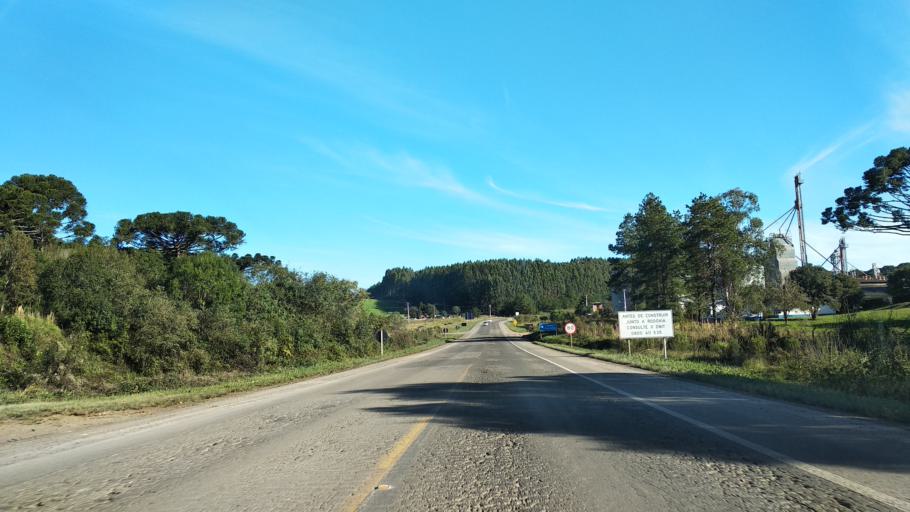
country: BR
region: Santa Catarina
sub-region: Campos Novos
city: Campos Novos
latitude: -27.3956
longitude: -51.1933
